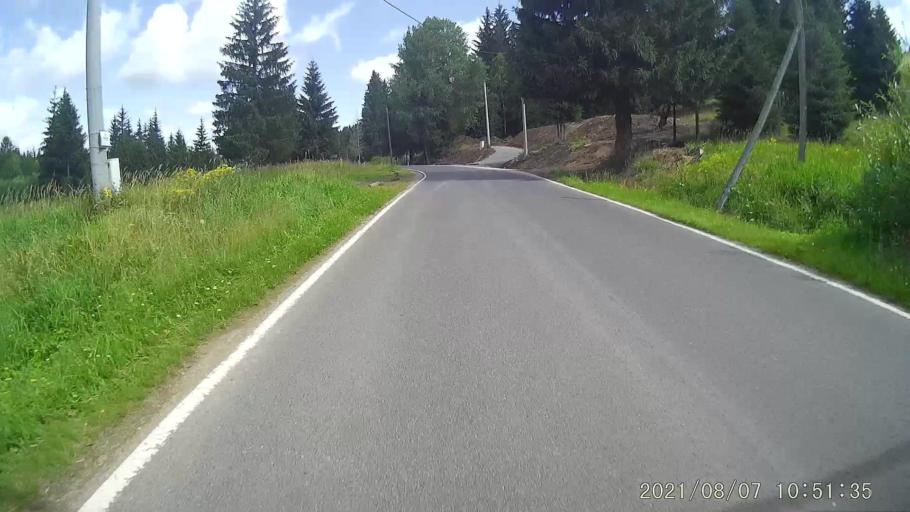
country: CZ
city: Rokytnice v Orlickych Horach
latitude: 50.2879
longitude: 16.4682
